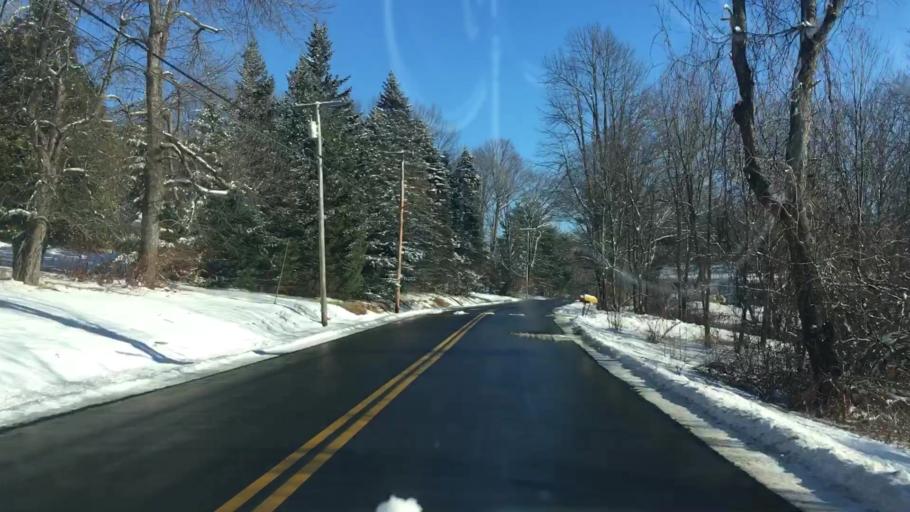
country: US
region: Maine
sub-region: Androscoggin County
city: Lisbon
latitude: 43.9491
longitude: -70.1443
